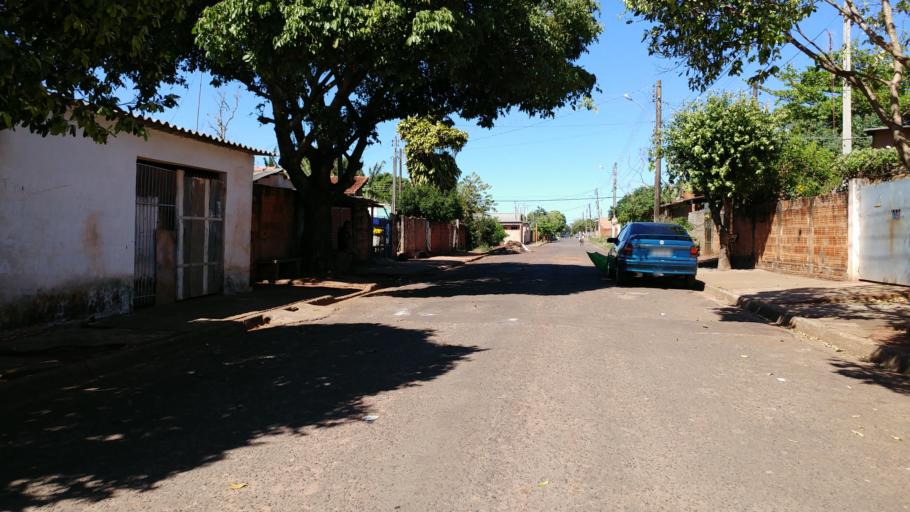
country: BR
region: Sao Paulo
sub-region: Paraguacu Paulista
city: Paraguacu Paulista
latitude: -22.4088
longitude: -50.5658
